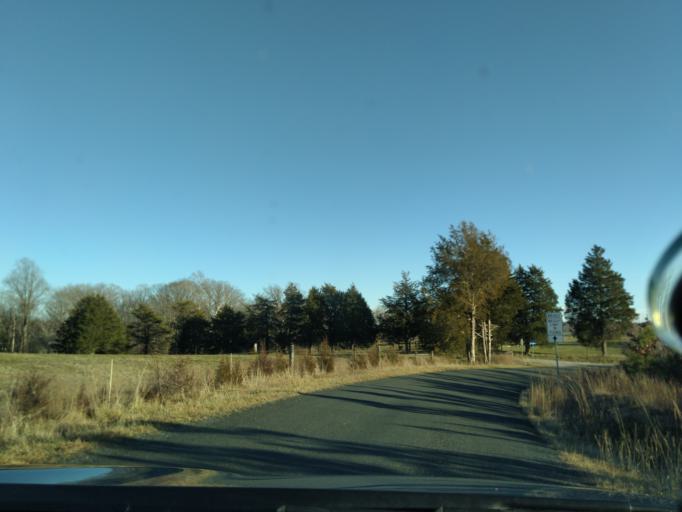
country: US
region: Virginia
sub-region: Prince Edward County
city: Hampden Sydney
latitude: 37.3583
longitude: -78.6035
